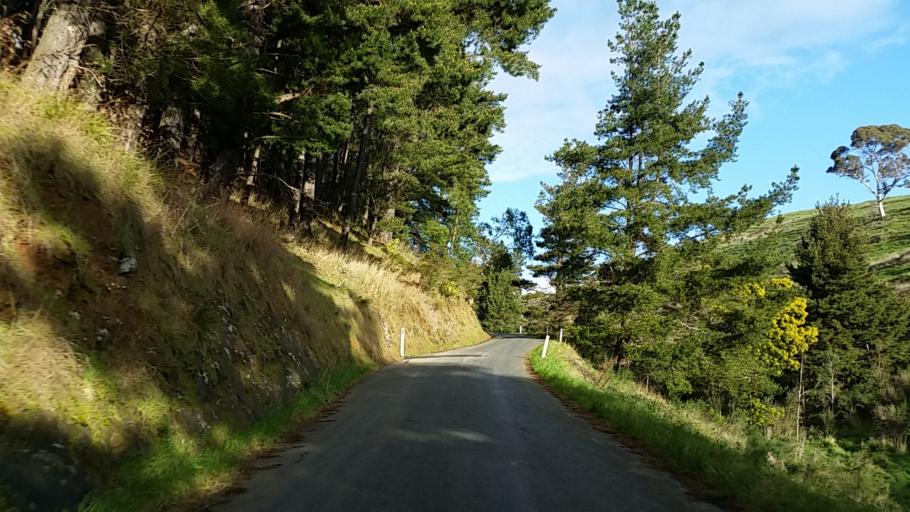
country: AU
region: South Australia
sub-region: Adelaide Hills
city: Adelaide Hills
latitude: -34.9268
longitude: 138.7705
